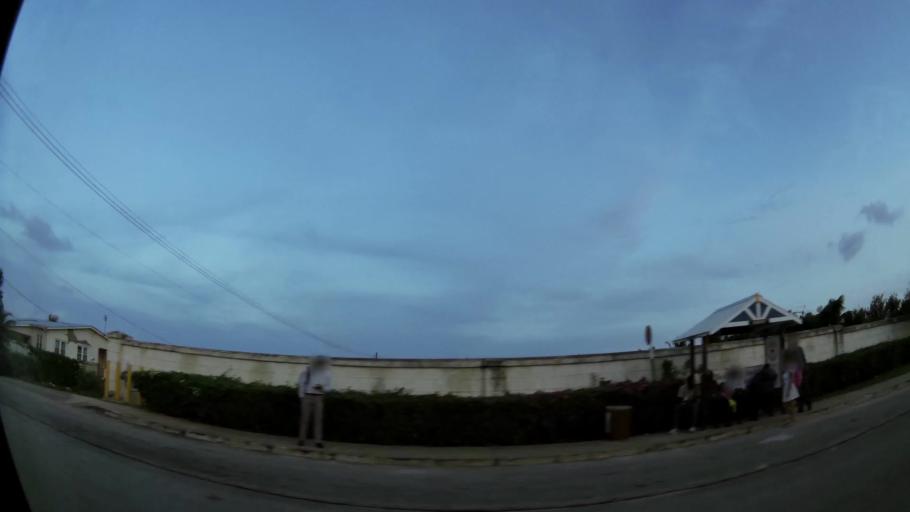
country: BB
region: Saint Philip
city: Crane
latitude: 13.1069
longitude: -59.4481
